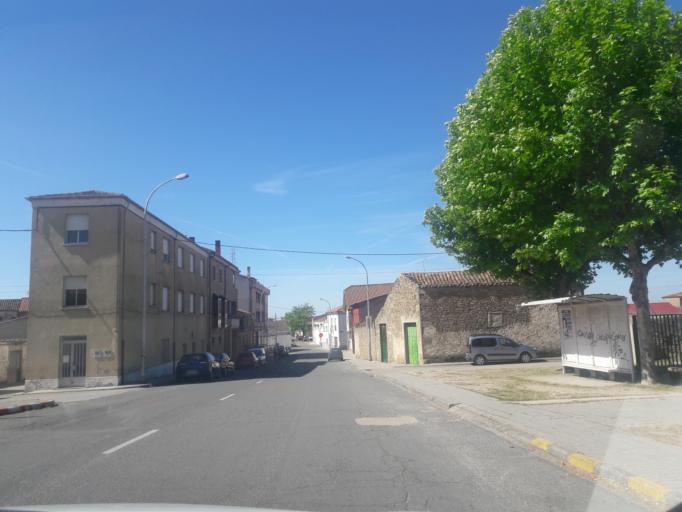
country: ES
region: Castille and Leon
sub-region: Provincia de Salamanca
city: Lumbrales
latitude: 40.9372
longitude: -6.7166
